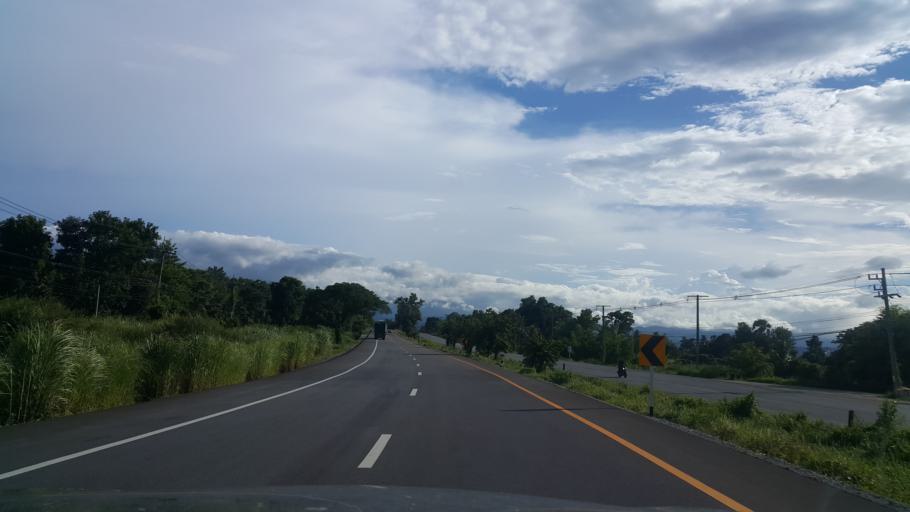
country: TH
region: Tak
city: Ban Tak
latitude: 17.1339
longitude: 99.1058
